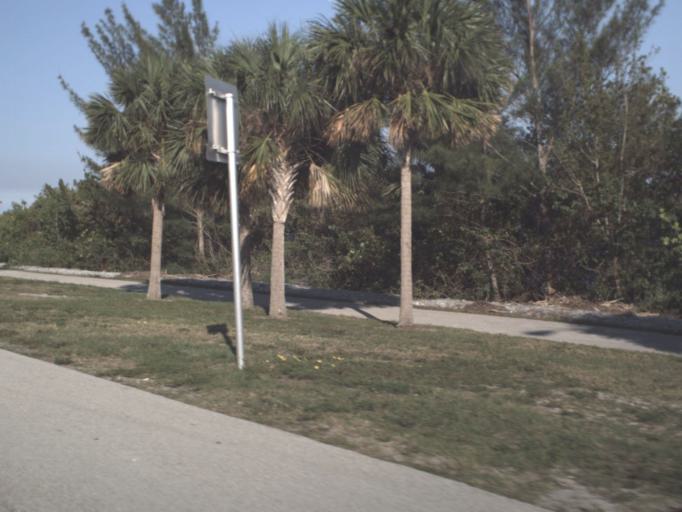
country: US
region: Florida
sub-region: Brevard County
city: Indialantic
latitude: 28.0863
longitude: -80.5850
